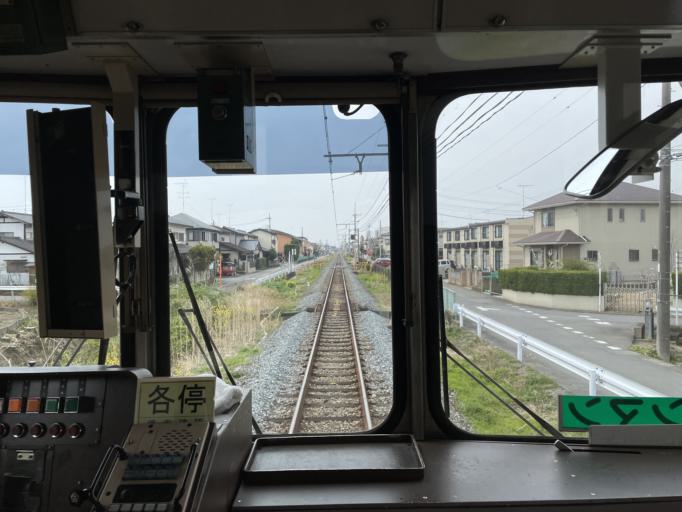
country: JP
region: Saitama
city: Gyoda
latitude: 36.1536
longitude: 139.4755
